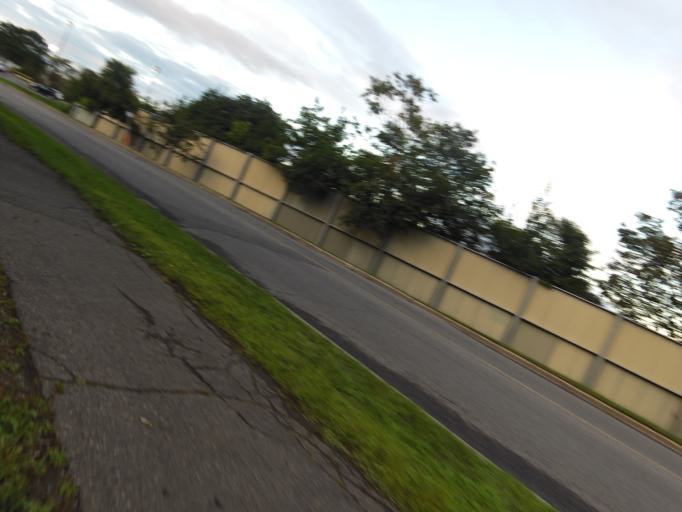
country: CA
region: Ontario
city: Bells Corners
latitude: 45.3493
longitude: -75.7927
